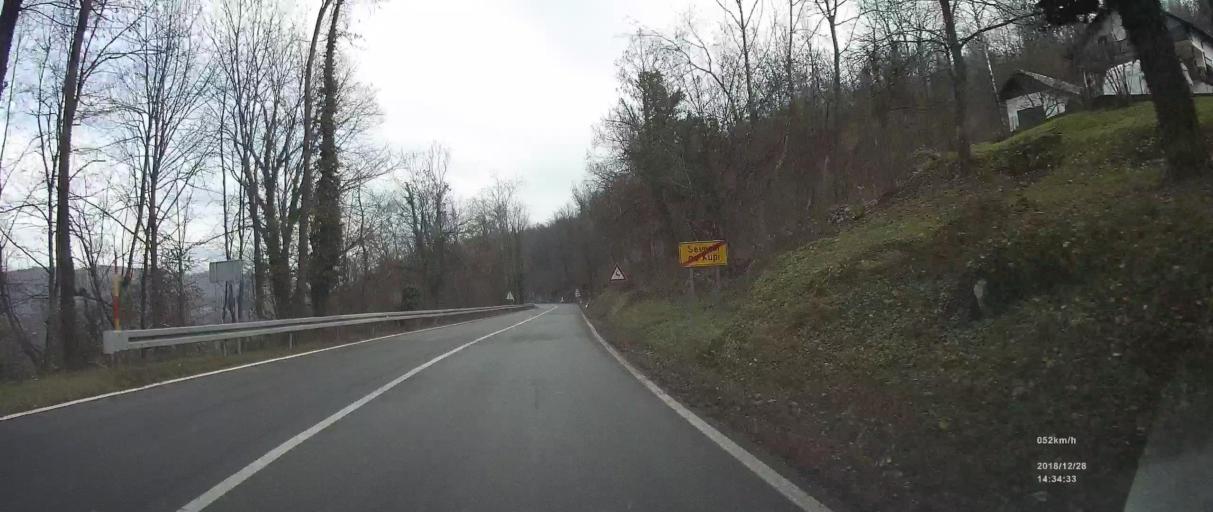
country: HR
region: Primorsko-Goranska
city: Vrbovsko
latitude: 45.4204
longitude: 15.1736
